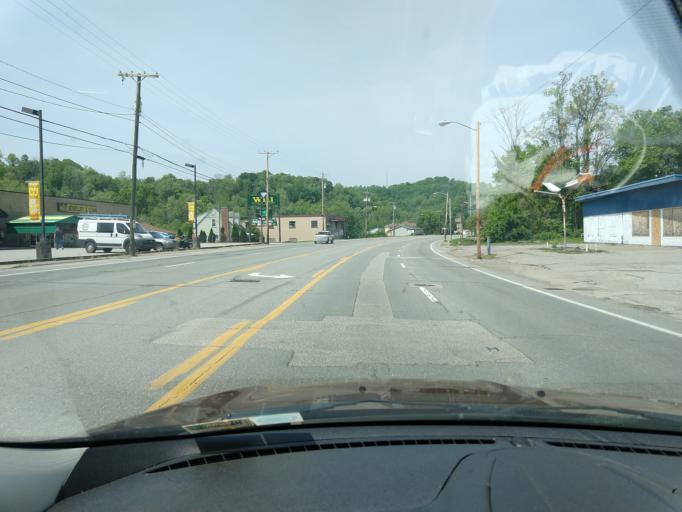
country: US
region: West Virginia
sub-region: Kanawha County
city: Dunbar
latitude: 38.3538
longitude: -81.7452
